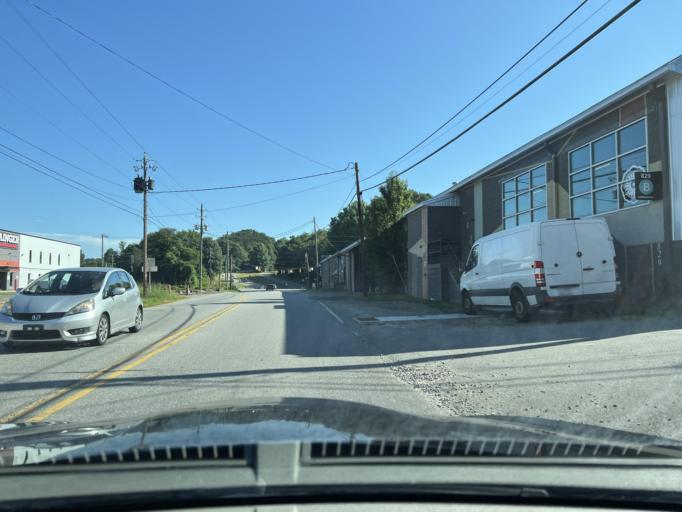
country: US
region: North Carolina
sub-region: Buncombe County
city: Woodfin
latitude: 35.6139
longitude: -82.5751
